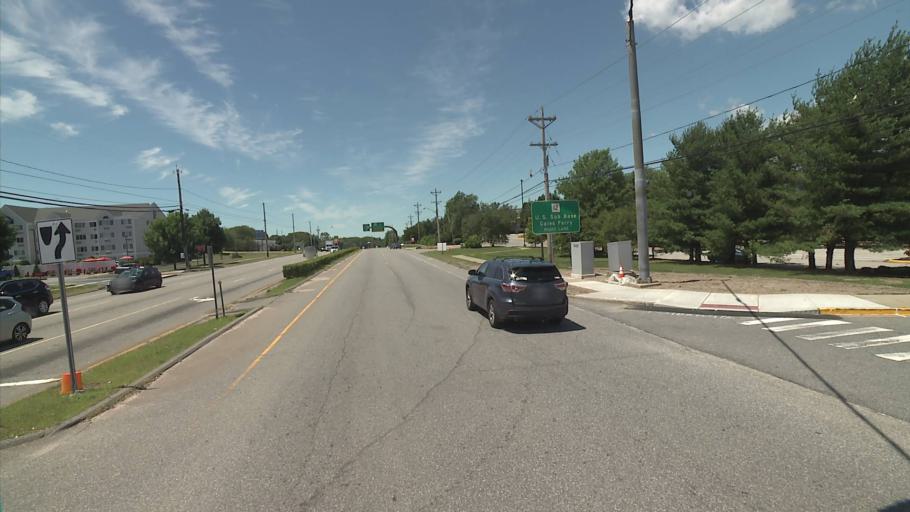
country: US
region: Connecticut
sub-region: New London County
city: Conning Towers-Nautilus Park
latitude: 41.3684
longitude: -72.0640
